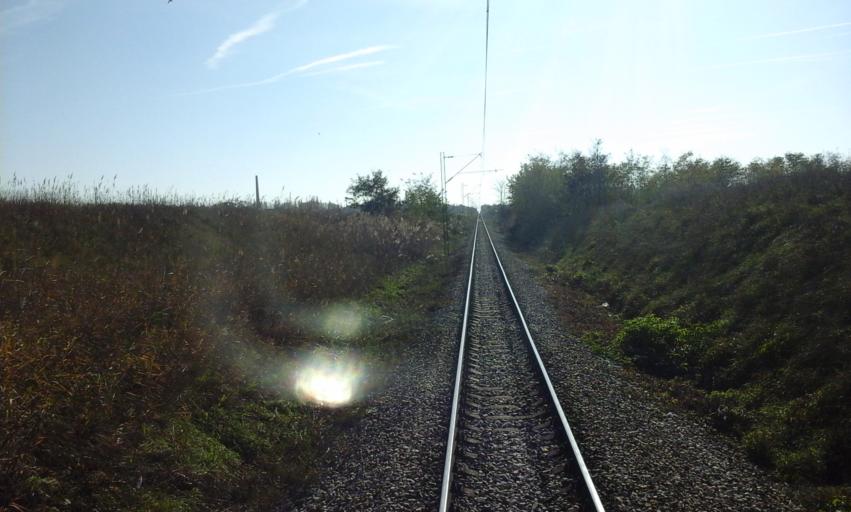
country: RS
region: Autonomna Pokrajina Vojvodina
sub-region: Severnobacki Okrug
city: Subotica
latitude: 46.0776
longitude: 19.6896
